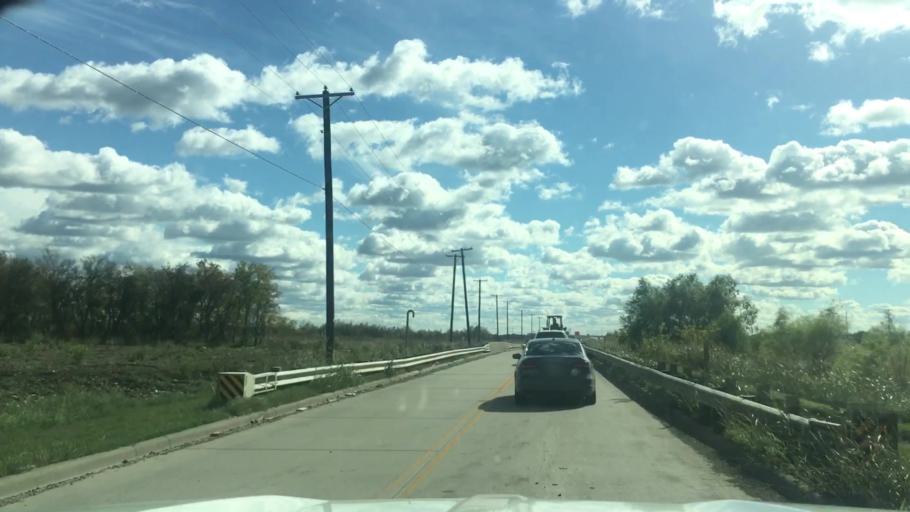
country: US
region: Texas
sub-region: Collin County
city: Prosper
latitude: 33.2308
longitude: -96.8189
